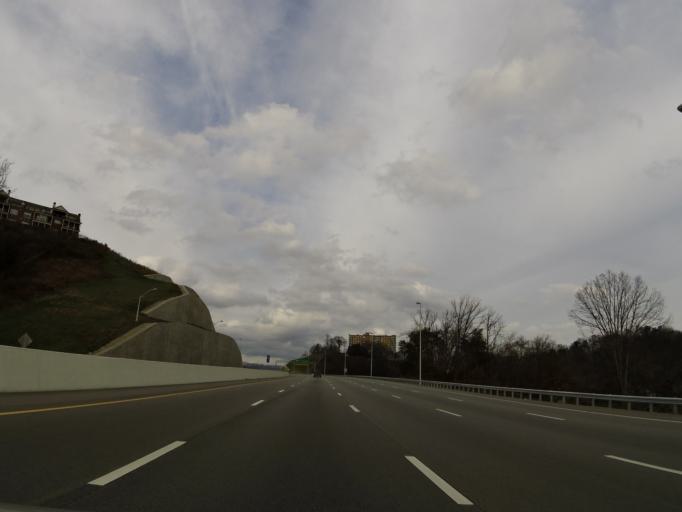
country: US
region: Tennessee
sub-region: Hamilton County
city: Chattanooga
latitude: 35.0674
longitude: -85.3191
